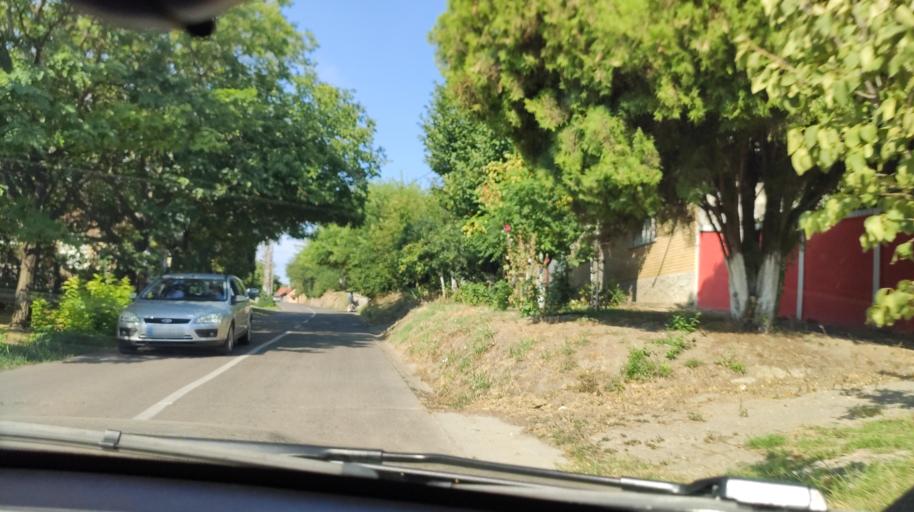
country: RS
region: Autonomna Pokrajina Vojvodina
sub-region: Severnobacki Okrug
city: Backa Topola
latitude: 45.8068
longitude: 19.6287
